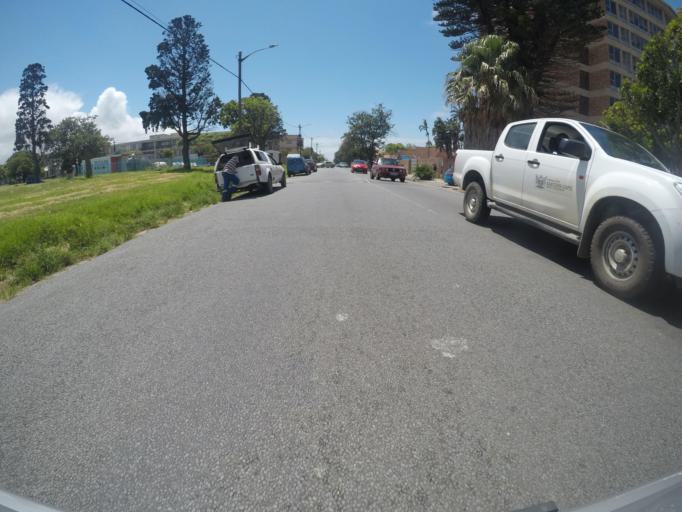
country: ZA
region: Eastern Cape
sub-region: Buffalo City Metropolitan Municipality
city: East London
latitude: -33.0029
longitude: 27.9018
